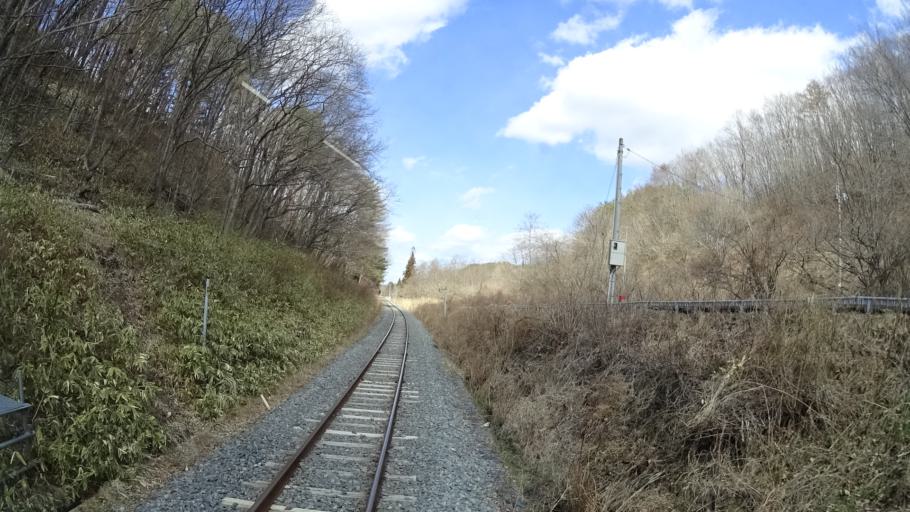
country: JP
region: Iwate
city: Yamada
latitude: 39.4946
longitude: 141.9276
